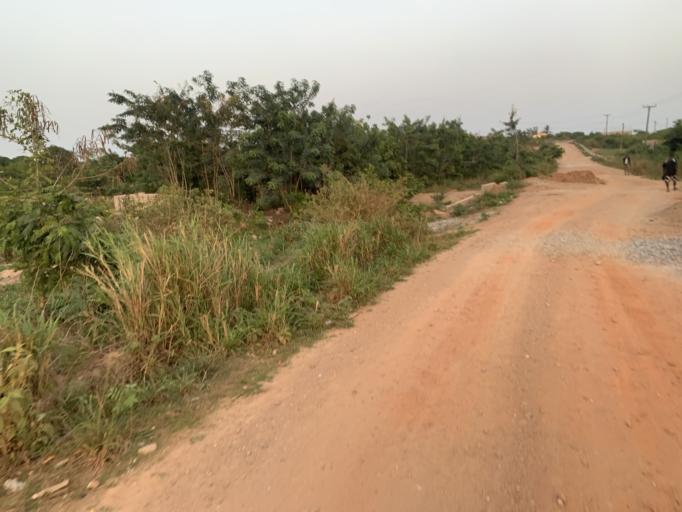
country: GH
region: Central
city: Winneba
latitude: 5.3765
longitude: -0.6098
